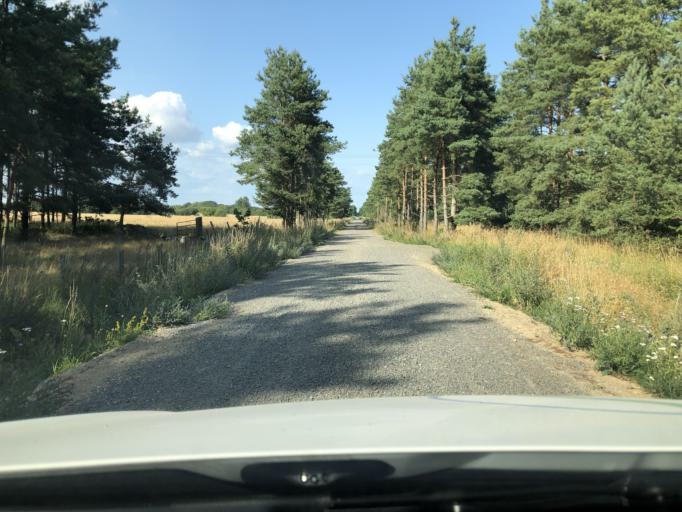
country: SE
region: Skane
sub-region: Kristianstads Kommun
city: Norra Asum
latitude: 55.9338
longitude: 14.1363
